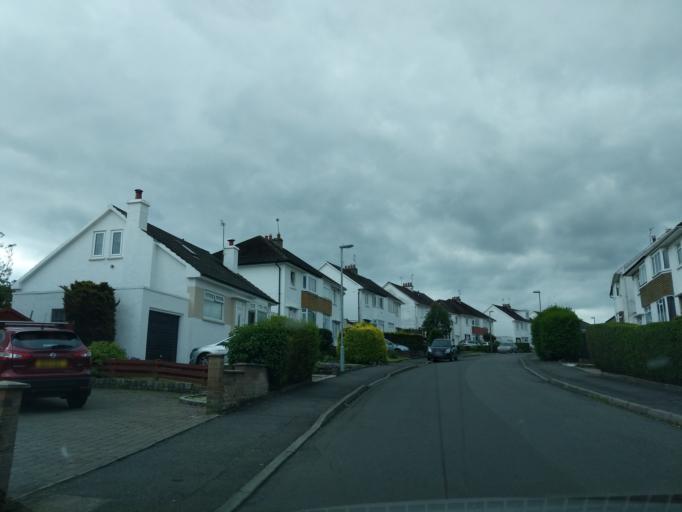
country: GB
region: Scotland
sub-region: Edinburgh
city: Colinton
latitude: 55.9693
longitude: -3.2666
